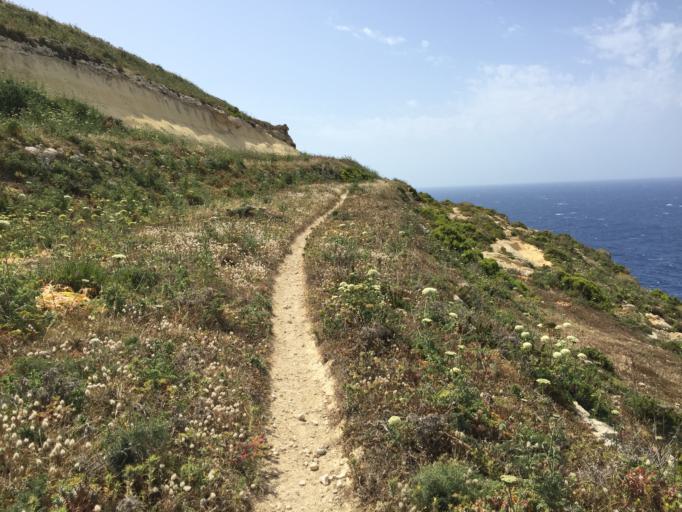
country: MT
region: L-Gharb
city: Gharb
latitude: 36.0740
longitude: 14.1975
